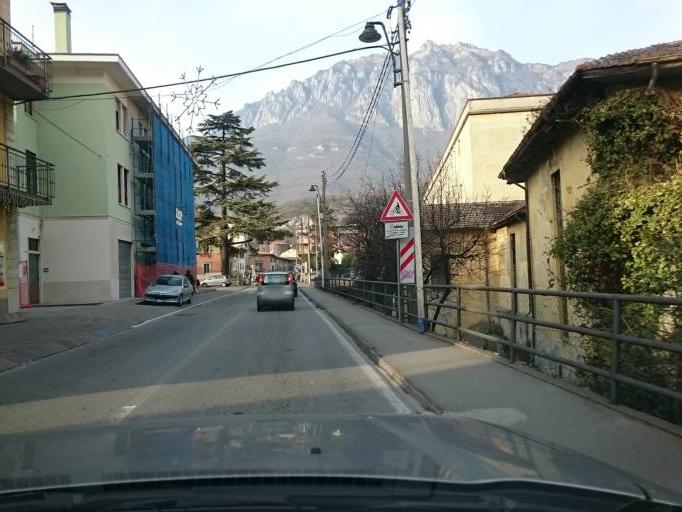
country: IT
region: Lombardy
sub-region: Provincia di Brescia
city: Darfo
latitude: 45.8819
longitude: 10.1818
